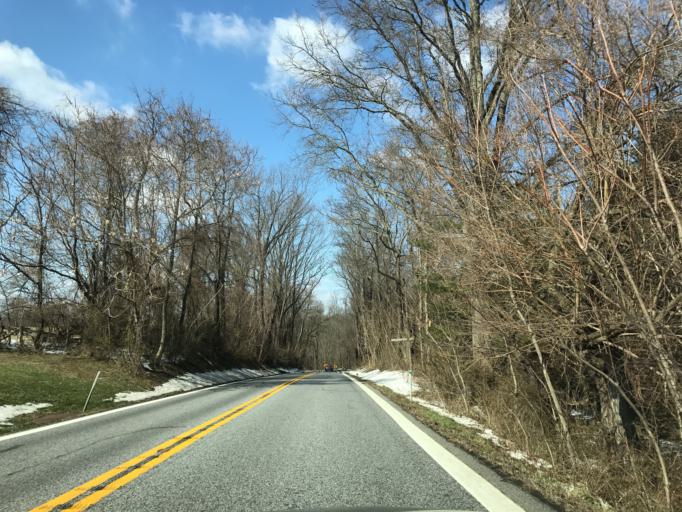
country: US
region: Maryland
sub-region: Baltimore County
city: Hunt Valley
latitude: 39.5110
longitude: -76.7144
